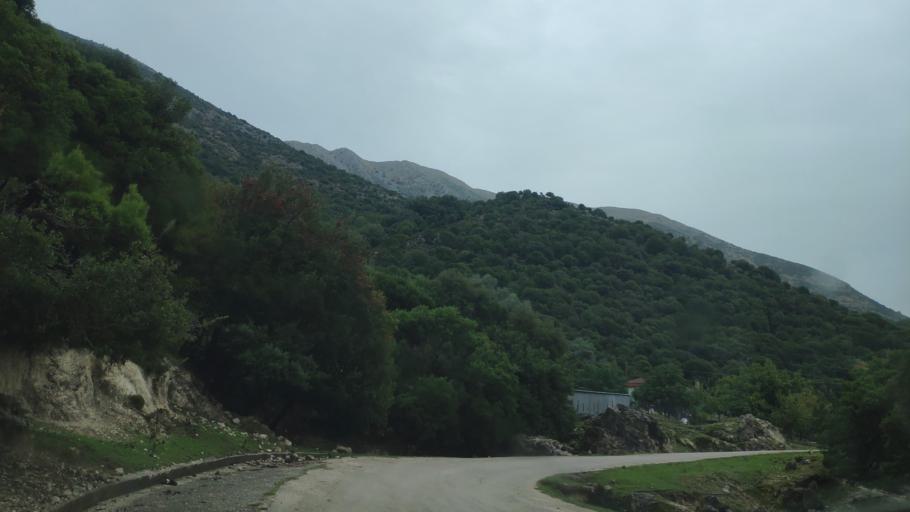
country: GR
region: Epirus
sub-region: Nomos Thesprotias
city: Paramythia
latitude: 39.3823
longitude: 20.6343
